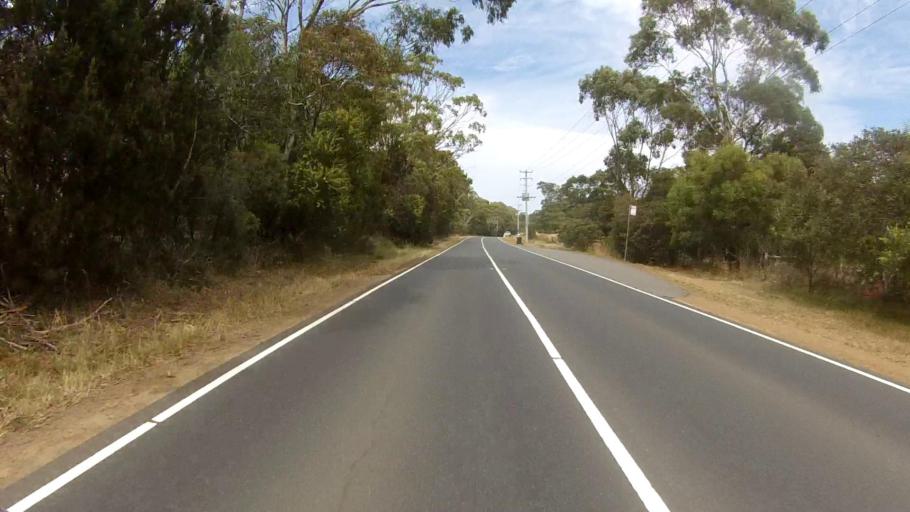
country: AU
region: Tasmania
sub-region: Clarence
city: Acton Park
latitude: -42.8751
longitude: 147.4829
